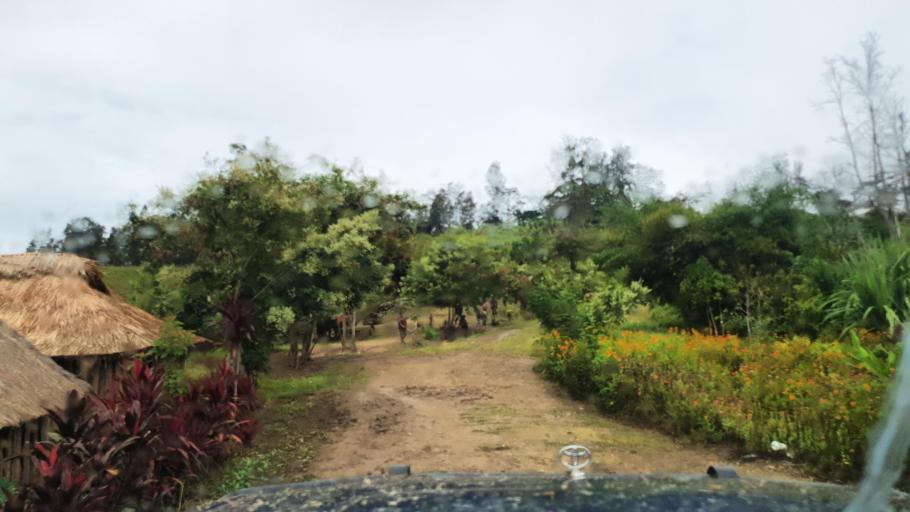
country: PG
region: Jiwaka
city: Minj
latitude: -5.9533
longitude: 144.7781
